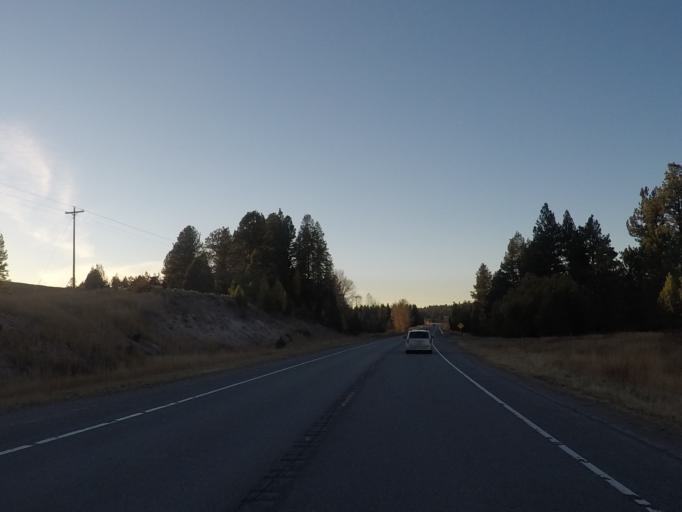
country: US
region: Montana
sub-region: Lewis and Clark County
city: Lincoln
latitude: 46.9984
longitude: -113.0324
